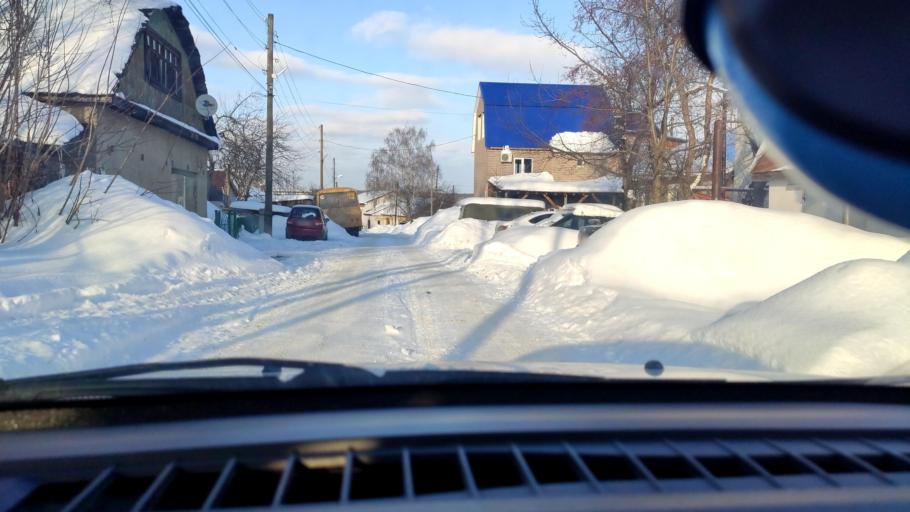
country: RU
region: Perm
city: Kultayevo
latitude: 57.9365
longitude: 55.8572
